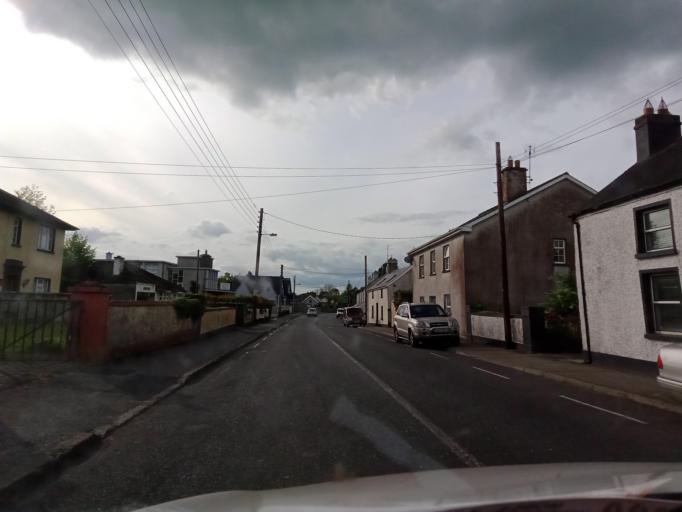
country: IE
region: Leinster
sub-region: Laois
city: Abbeyleix
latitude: 52.9143
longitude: -7.3504
